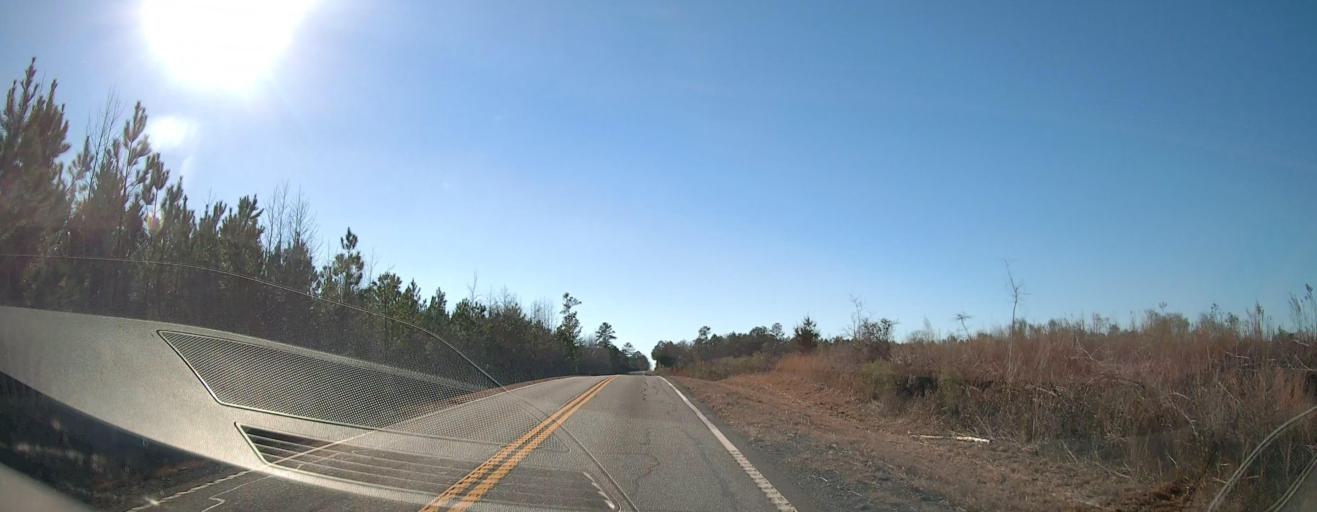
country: US
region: Georgia
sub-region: Talbot County
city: Talbotton
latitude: 32.6723
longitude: -84.4771
